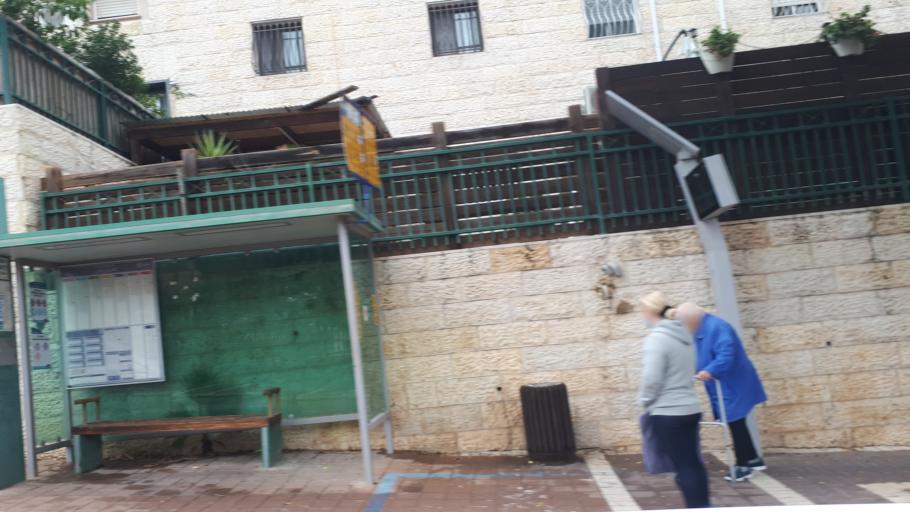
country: IL
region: Central District
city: Modiin
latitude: 31.9049
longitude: 35.0079
